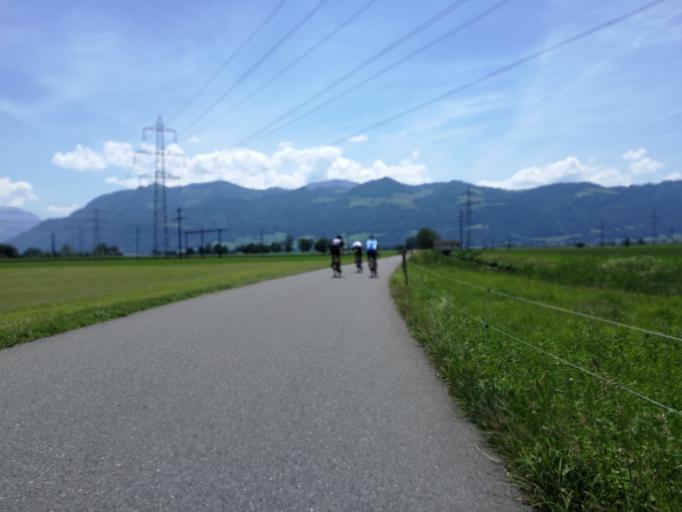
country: CH
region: Saint Gallen
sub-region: Wahlkreis See-Gaster
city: Uznach
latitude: 47.2149
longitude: 8.9705
